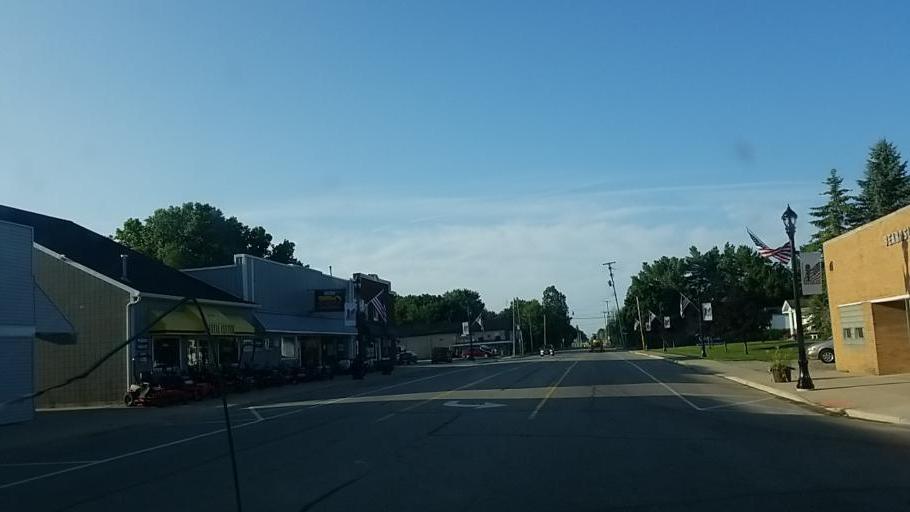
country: US
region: Michigan
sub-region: Montcalm County
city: Stanton
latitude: 43.2120
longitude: -85.0736
